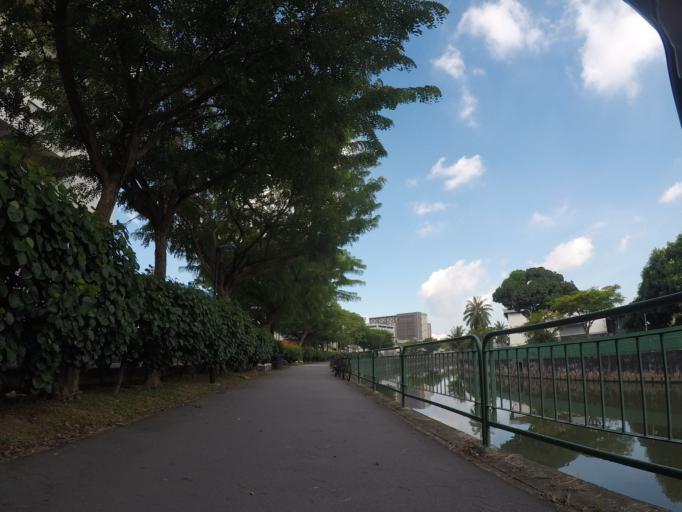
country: MY
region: Johor
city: Johor Bahru
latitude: 1.3382
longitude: 103.7150
